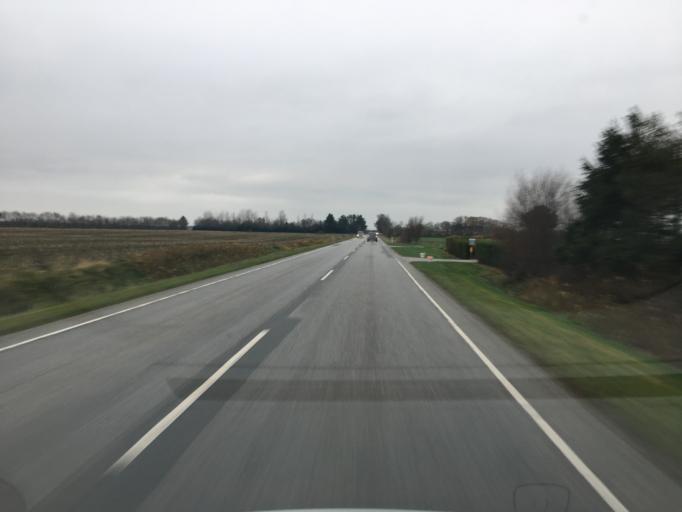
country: DK
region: South Denmark
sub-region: Aabenraa Kommune
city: Tinglev
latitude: 54.9891
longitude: 9.1823
